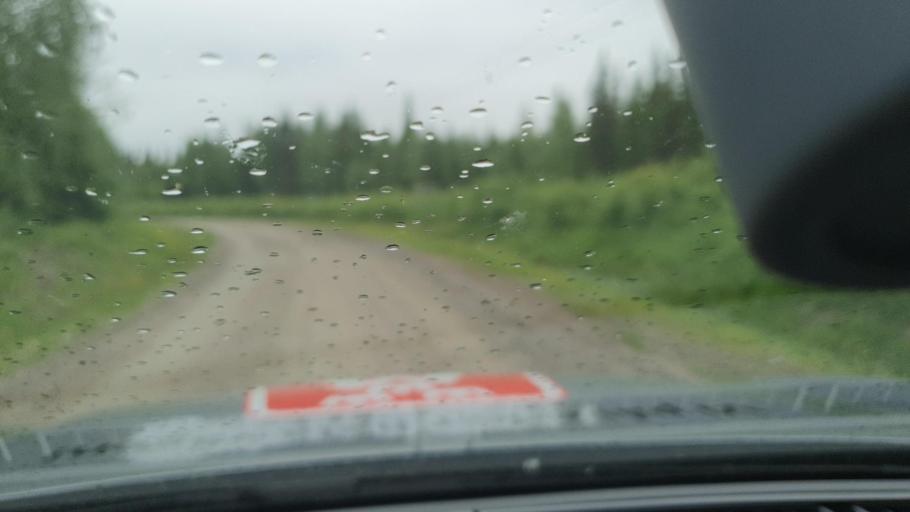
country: SE
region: Norrbotten
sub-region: Kalix Kommun
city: Rolfs
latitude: 66.0704
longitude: 22.9813
